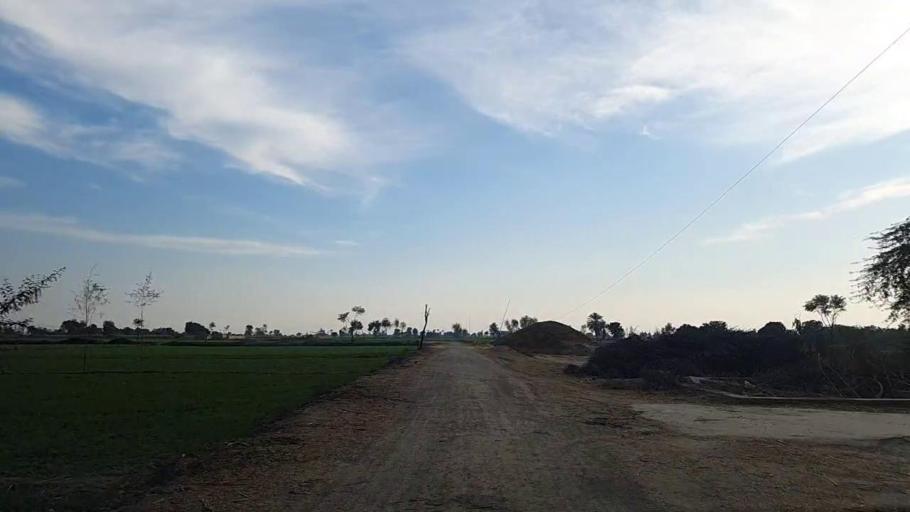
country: PK
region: Sindh
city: Bandhi
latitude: 26.5590
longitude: 68.2784
